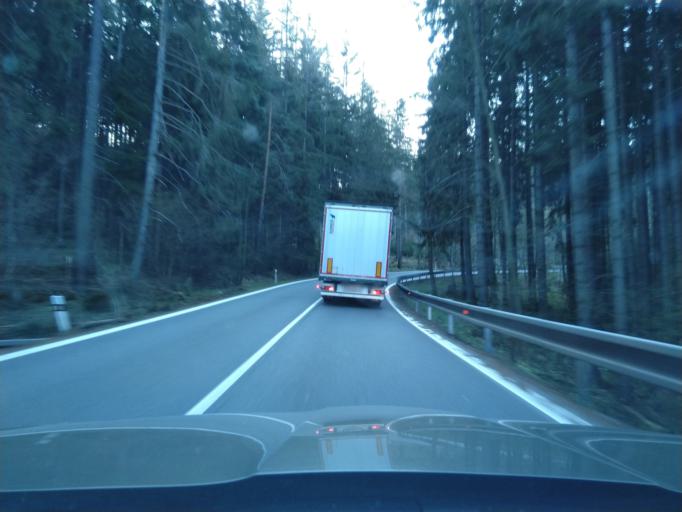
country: CZ
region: Jihocesky
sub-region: Okres Prachatice
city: Vimperk
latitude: 49.0393
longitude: 13.7627
